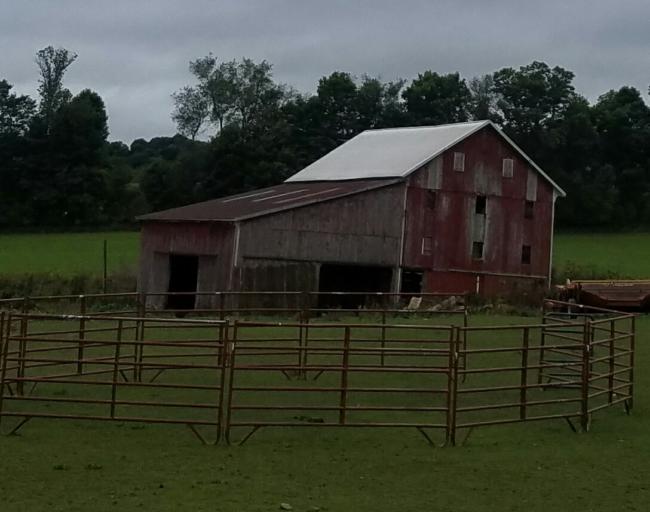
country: US
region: Ohio
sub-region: Ashland County
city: Loudonville
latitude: 40.5563
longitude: -82.3020
